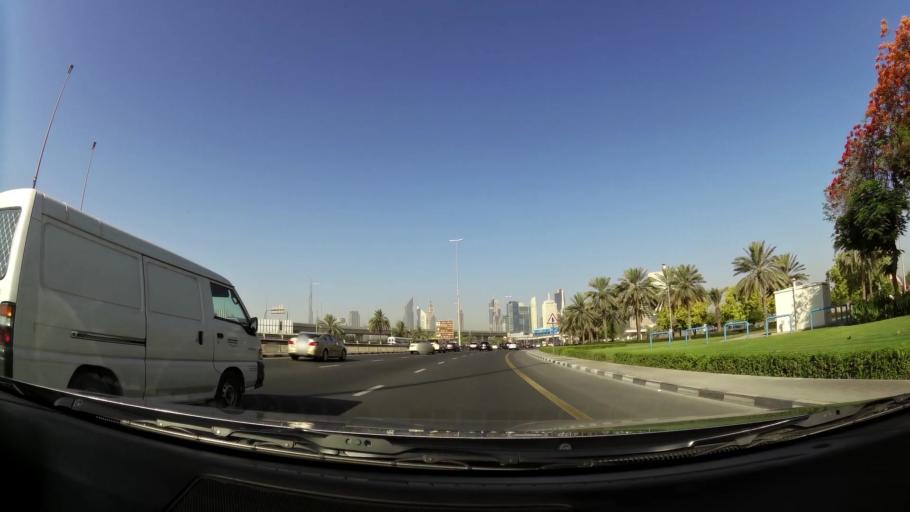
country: AE
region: Ash Shariqah
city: Sharjah
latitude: 25.2332
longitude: 55.3025
